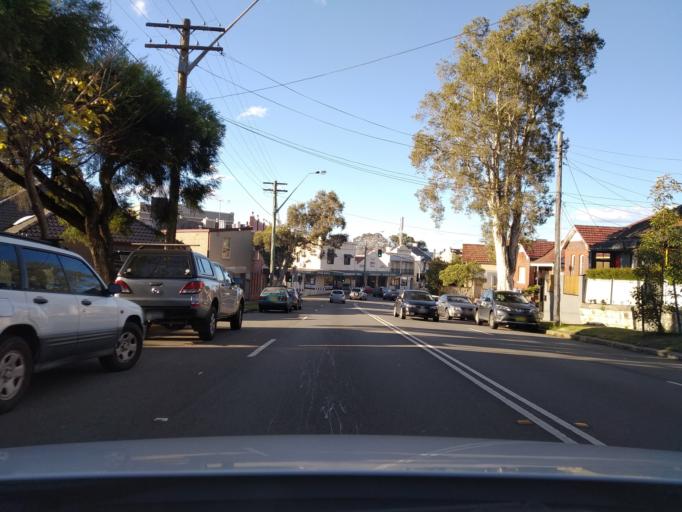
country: AU
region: New South Wales
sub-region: Ashfield
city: Summer Hill
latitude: -33.8960
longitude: 151.1380
